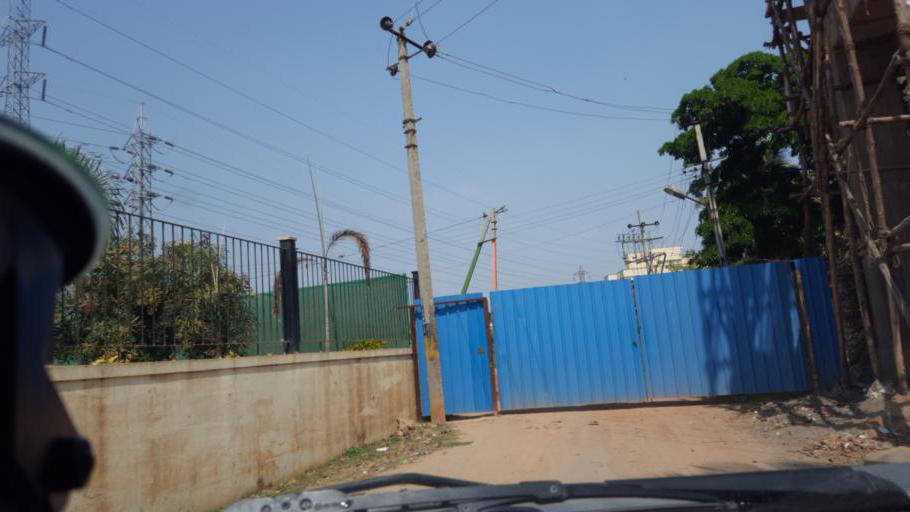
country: IN
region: Karnataka
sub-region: Bangalore Urban
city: Bangalore
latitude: 12.9773
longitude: 77.6720
